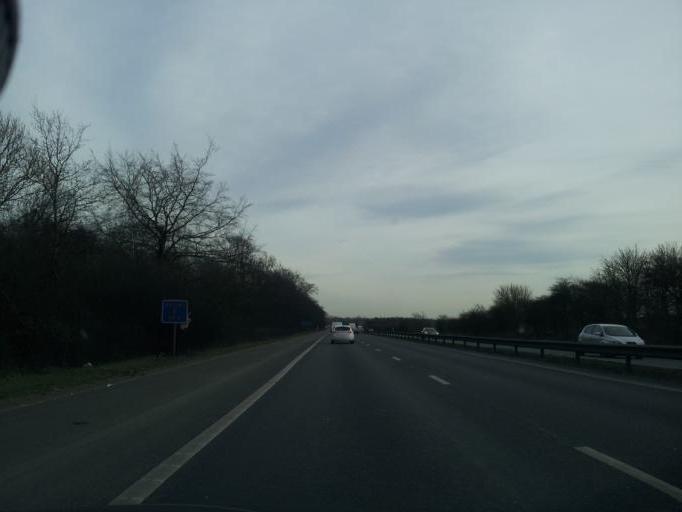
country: GB
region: England
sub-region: Hertfordshire
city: Hatfield
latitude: 51.7336
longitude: -0.2340
